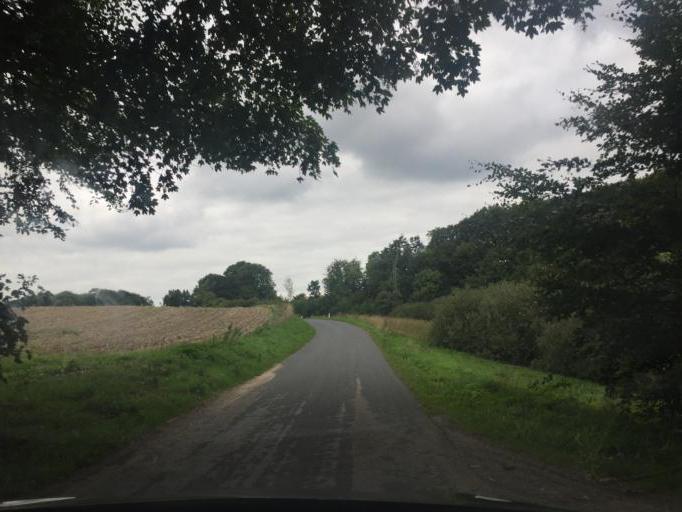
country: DK
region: South Denmark
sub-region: Assens Kommune
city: Tommerup
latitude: 55.3572
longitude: 10.2256
